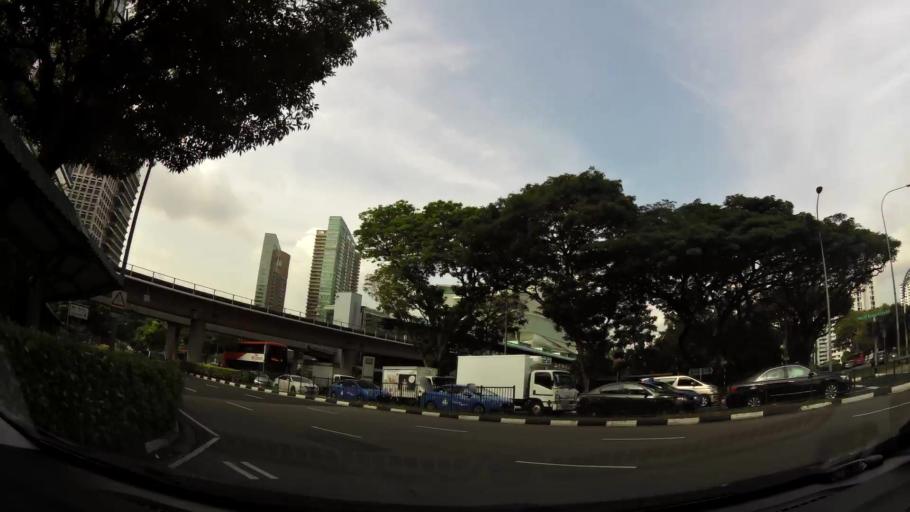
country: SG
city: Singapore
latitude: 1.3076
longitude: 103.7912
